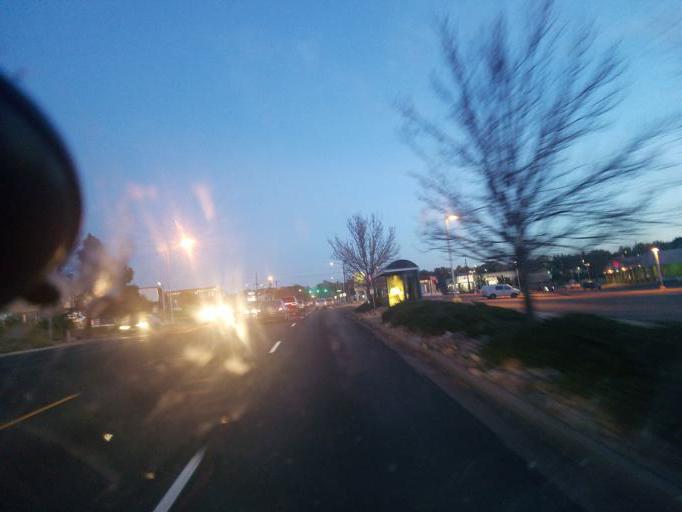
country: US
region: Colorado
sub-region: El Paso County
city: Colorado Springs
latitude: 38.8236
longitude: -104.7805
